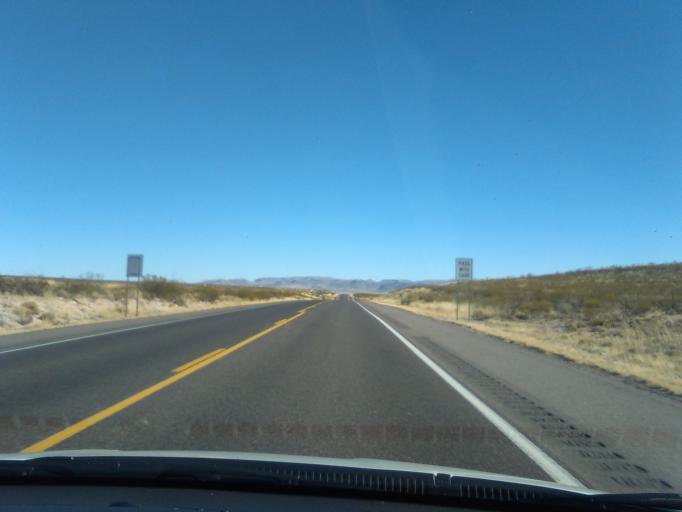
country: US
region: New Mexico
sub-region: Dona Ana County
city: Hatch
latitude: 32.5750
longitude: -107.4194
